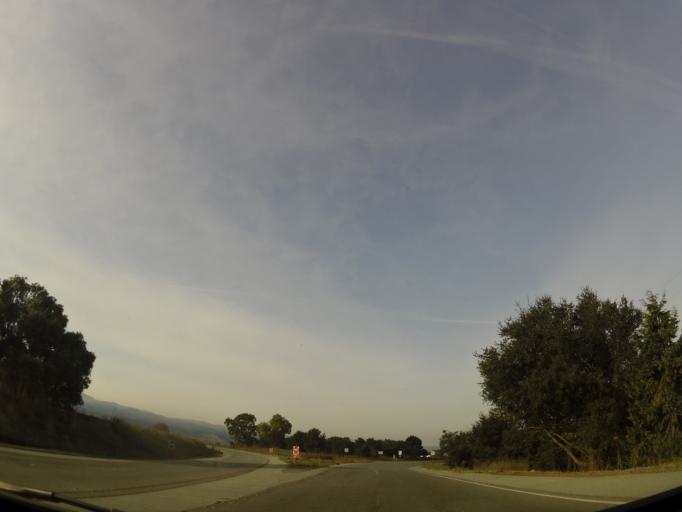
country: US
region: California
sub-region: San Benito County
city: Hollister
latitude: 36.8523
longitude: -121.4486
